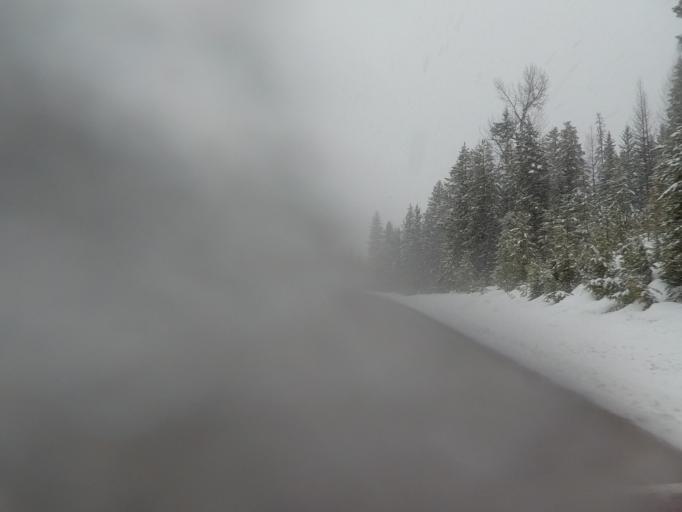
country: US
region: Montana
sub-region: Missoula County
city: Seeley Lake
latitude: 47.4381
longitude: -113.6704
